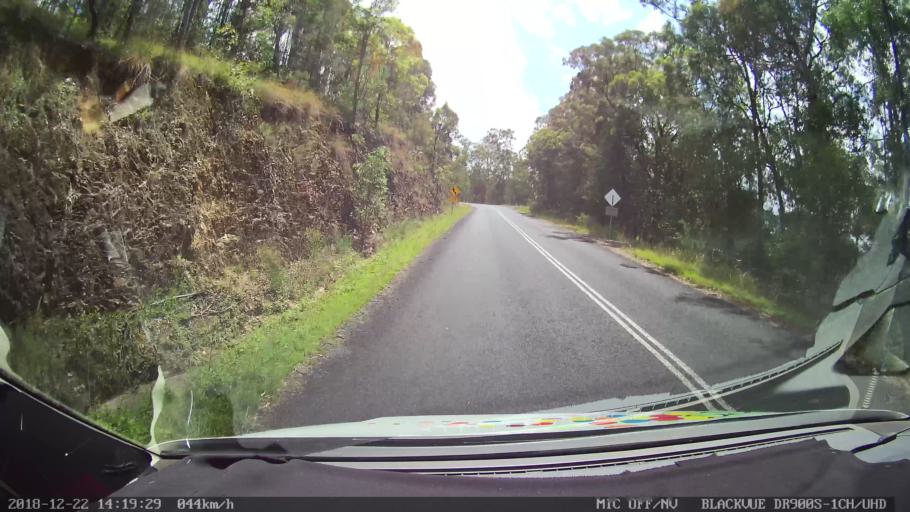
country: AU
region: New South Wales
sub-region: Clarence Valley
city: Coutts Crossing
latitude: -30.0103
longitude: 152.6630
